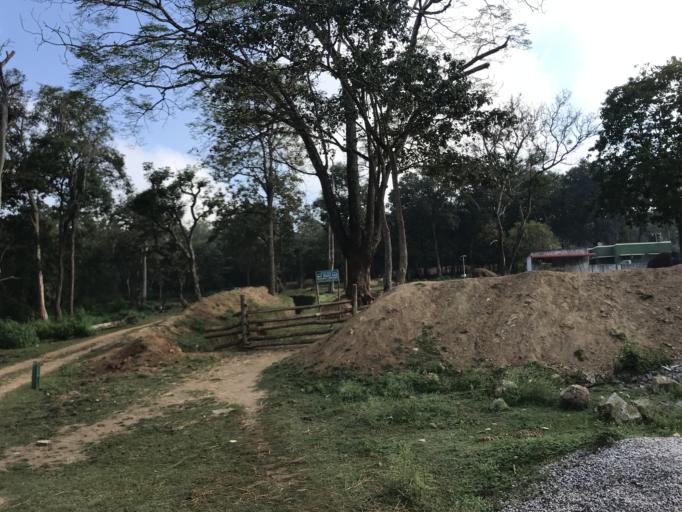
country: IN
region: Karnataka
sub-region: Mysore
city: Heggadadevankote
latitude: 11.9352
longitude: 76.1968
